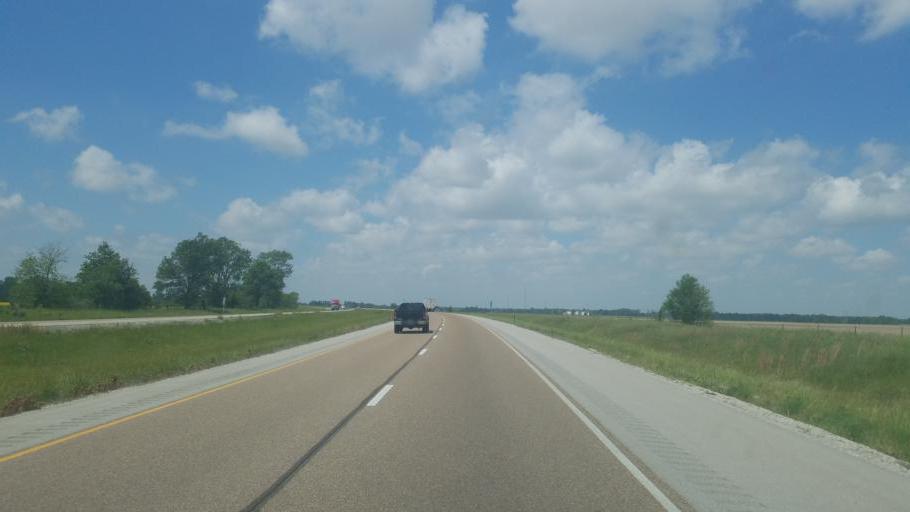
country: US
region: Illinois
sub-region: Clark County
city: Casey
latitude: 39.2826
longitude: -88.0690
